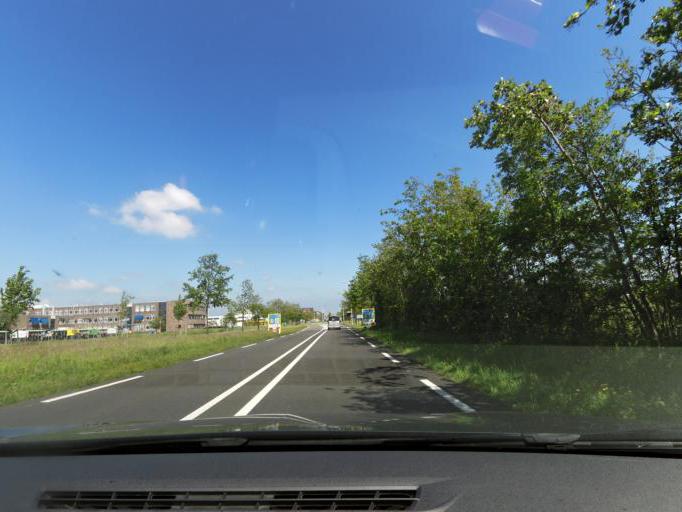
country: NL
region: South Holland
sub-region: Gemeente Hellevoetsluis
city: Nieuw-Helvoet
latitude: 51.8331
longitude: 4.1172
